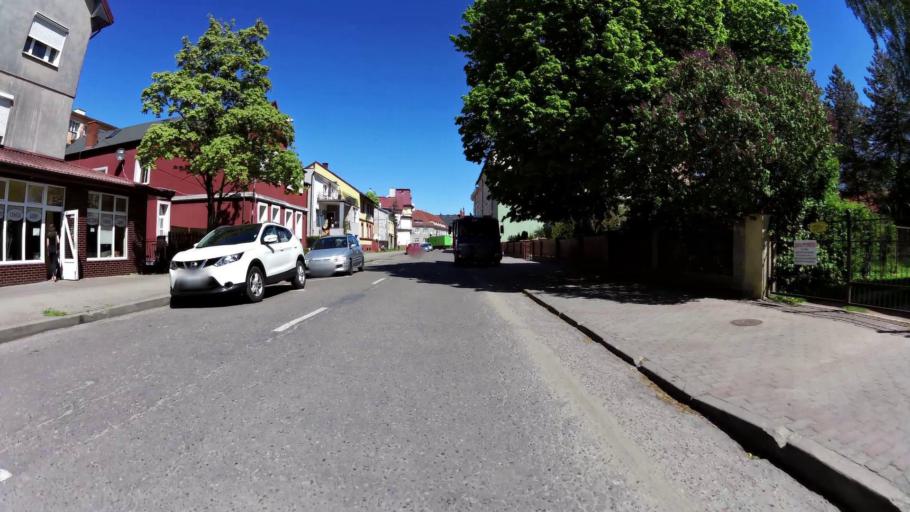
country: PL
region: West Pomeranian Voivodeship
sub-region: Powiat slawienski
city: Darlowo
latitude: 54.4176
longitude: 16.4059
